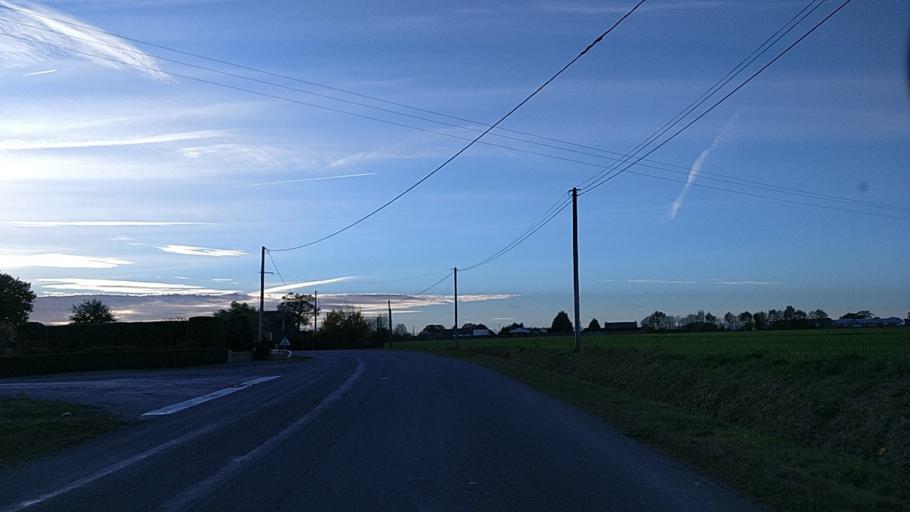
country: FR
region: Brittany
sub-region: Departement d'Ille-et-Vilaine
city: Chevaigne
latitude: 48.2126
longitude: -1.6195
